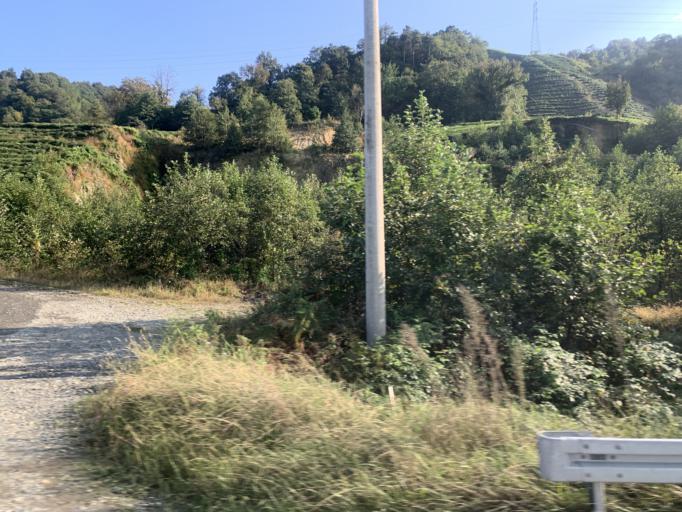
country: TR
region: Trabzon
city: Of
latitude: 40.9338
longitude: 40.2432
